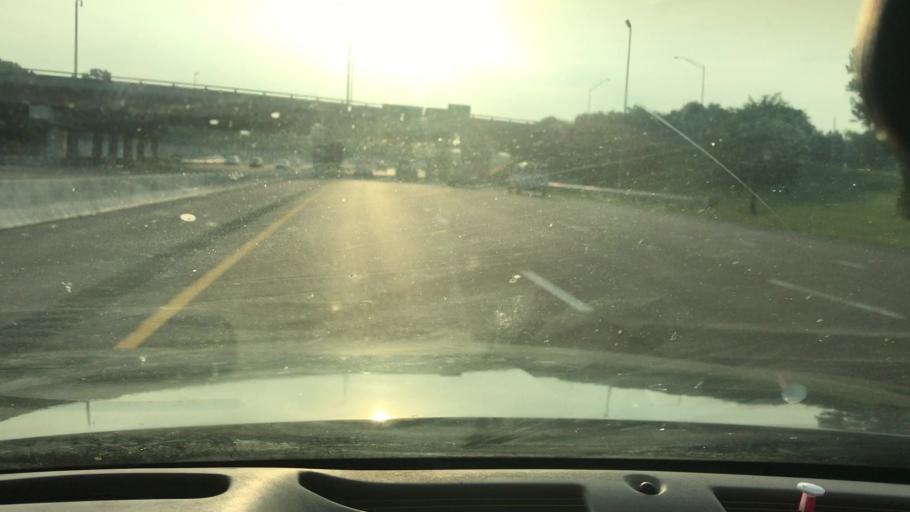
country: US
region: Tennessee
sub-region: Shelby County
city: Germantown
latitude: 35.0830
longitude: -89.8941
